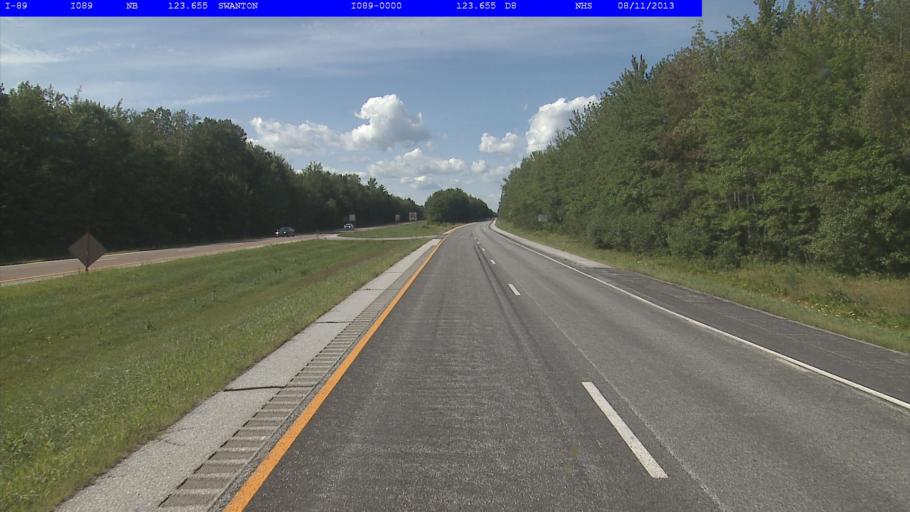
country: US
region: Vermont
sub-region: Franklin County
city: Swanton
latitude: 44.9262
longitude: -73.1094
